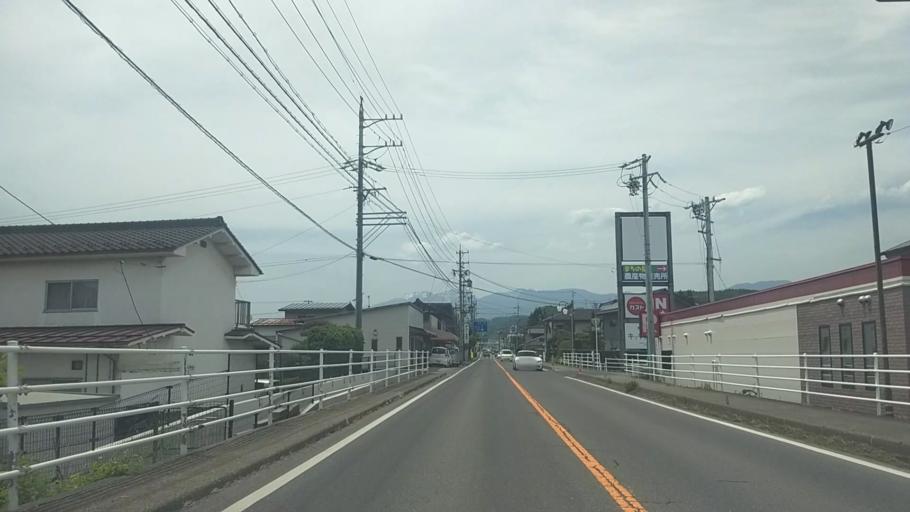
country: JP
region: Nagano
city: Saku
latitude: 36.1655
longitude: 138.4857
